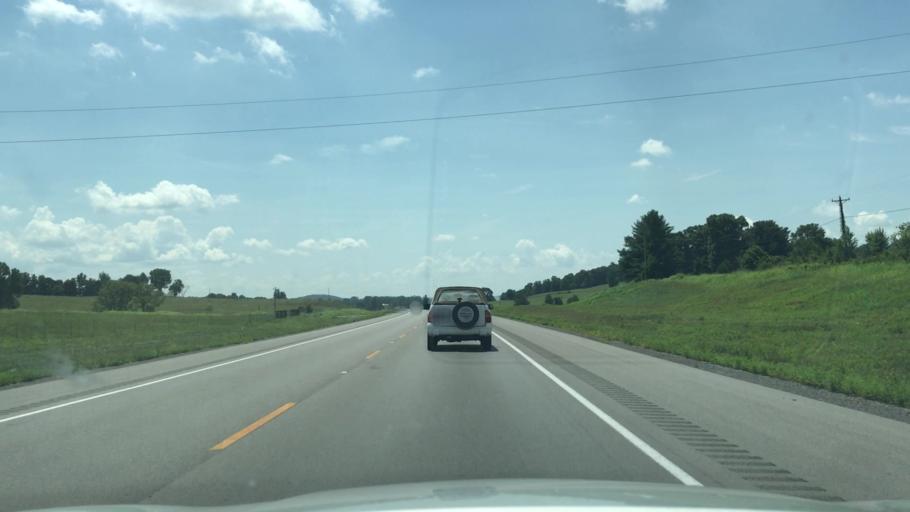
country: US
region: Kentucky
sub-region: Clinton County
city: Albany
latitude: 36.6377
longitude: -85.0997
